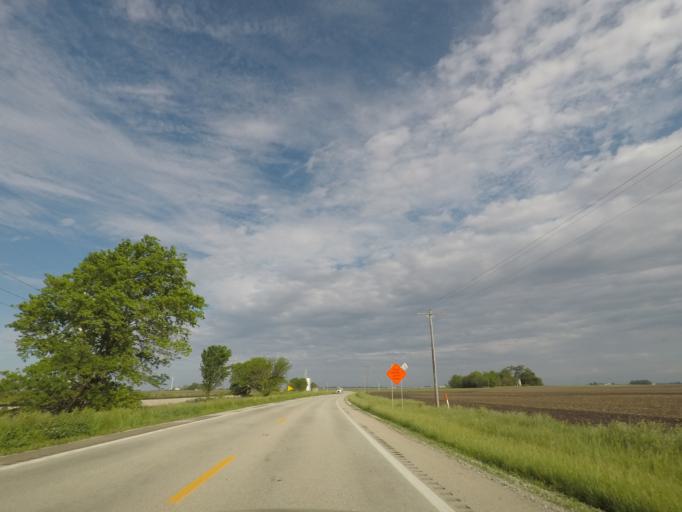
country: US
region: Illinois
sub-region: Logan County
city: Mount Pulaski
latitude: 39.9831
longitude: -89.2162
